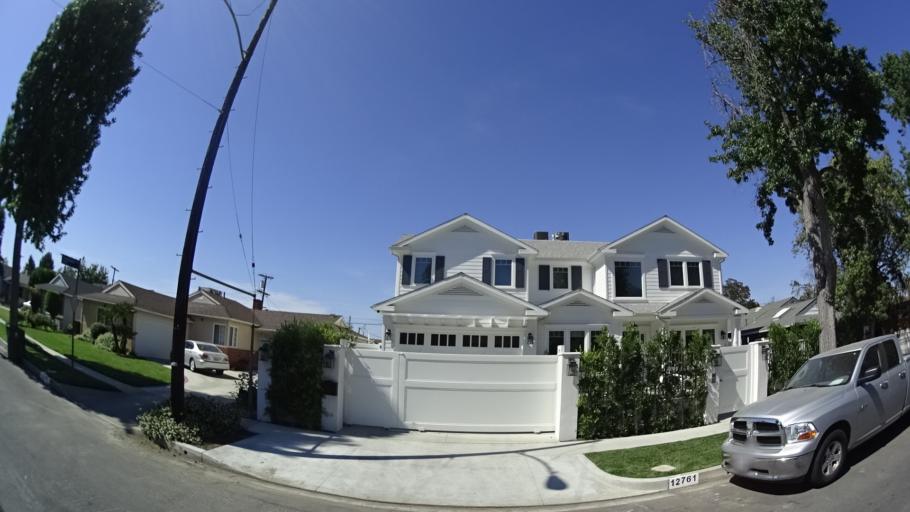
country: US
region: California
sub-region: Los Angeles County
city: North Hollywood
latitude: 34.1695
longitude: -118.4115
